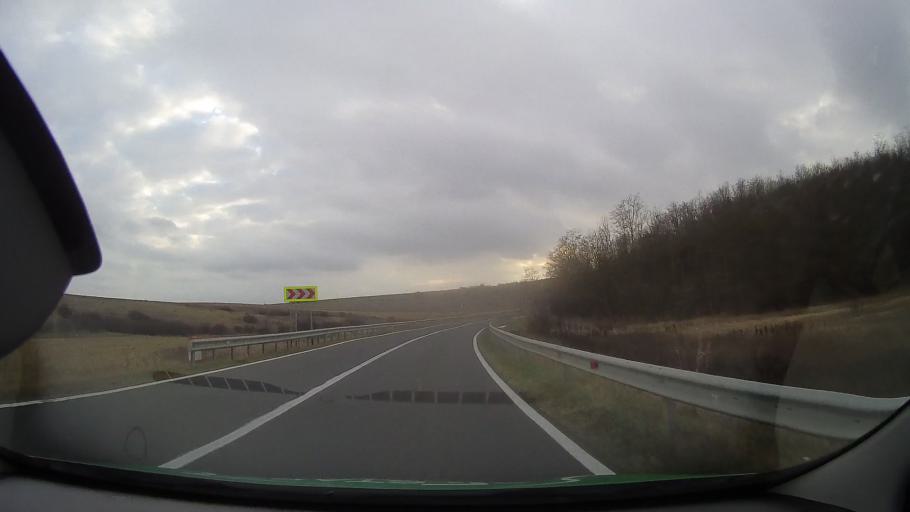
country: RO
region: Constanta
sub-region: Comuna Deleni
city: Deleni
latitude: 44.1007
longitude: 28.0229
